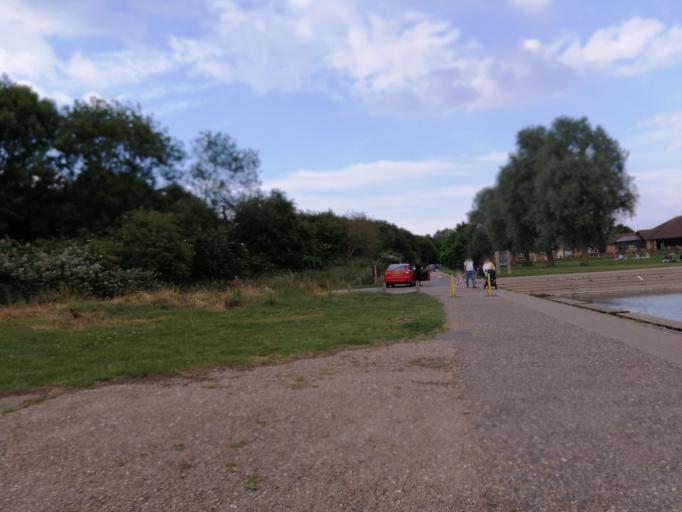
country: GB
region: England
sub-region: Peterborough
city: Peterborough
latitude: 52.5700
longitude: -0.2700
